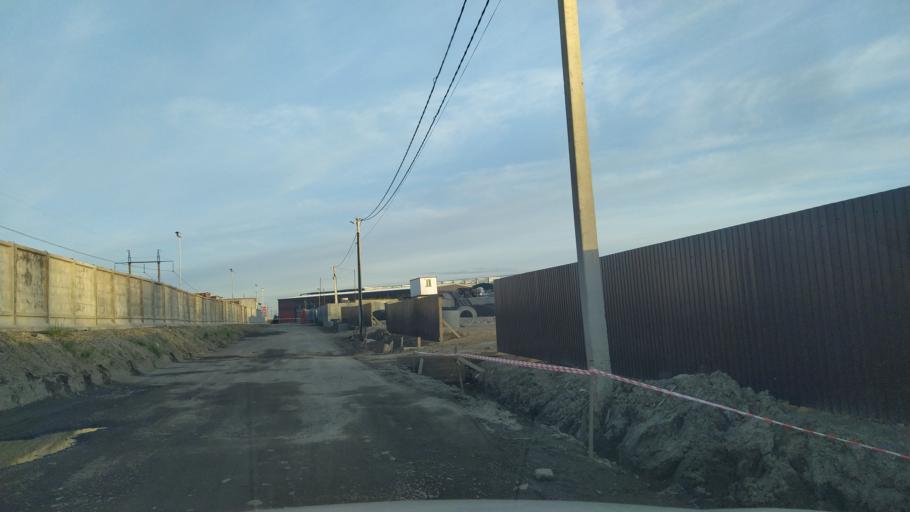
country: RU
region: St.-Petersburg
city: Obukhovo
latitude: 59.8036
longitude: 30.4599
